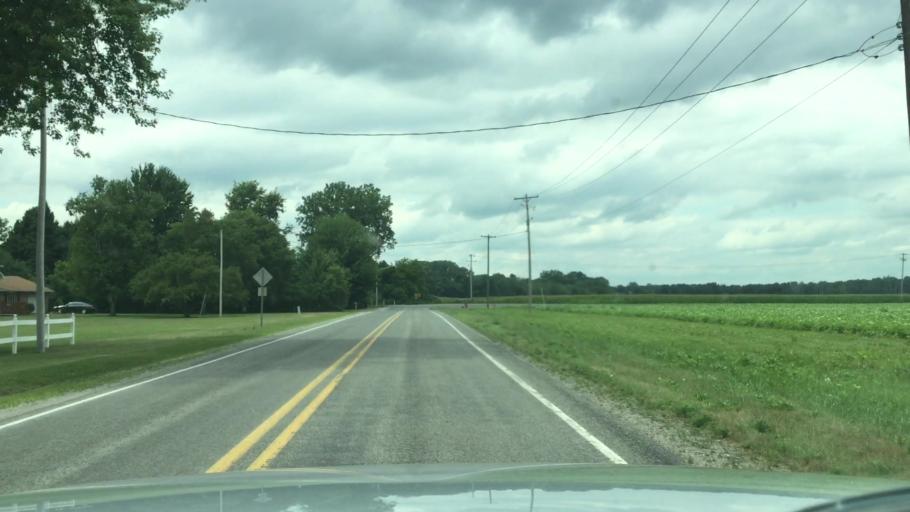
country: US
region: Michigan
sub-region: Saginaw County
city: Burt
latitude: 43.2813
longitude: -83.8919
